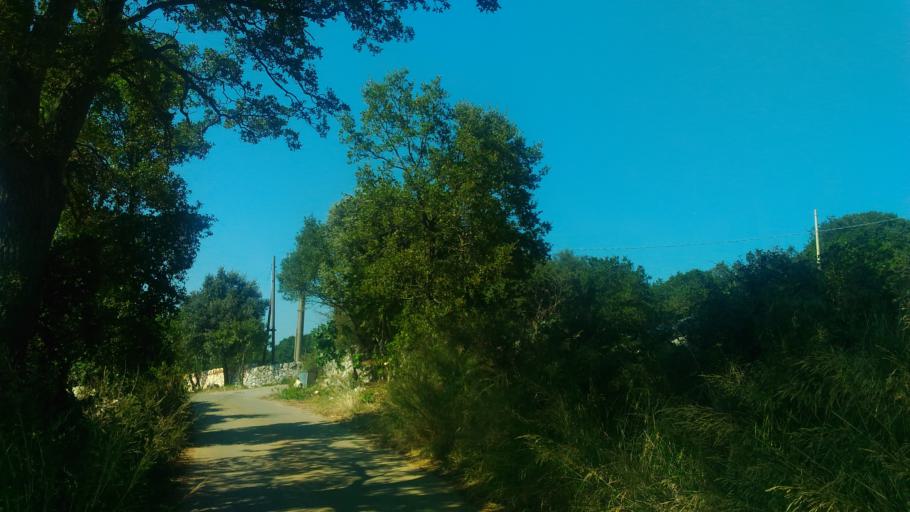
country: IT
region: Apulia
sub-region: Provincia di Bari
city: Noci
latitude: 40.8146
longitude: 17.1791
